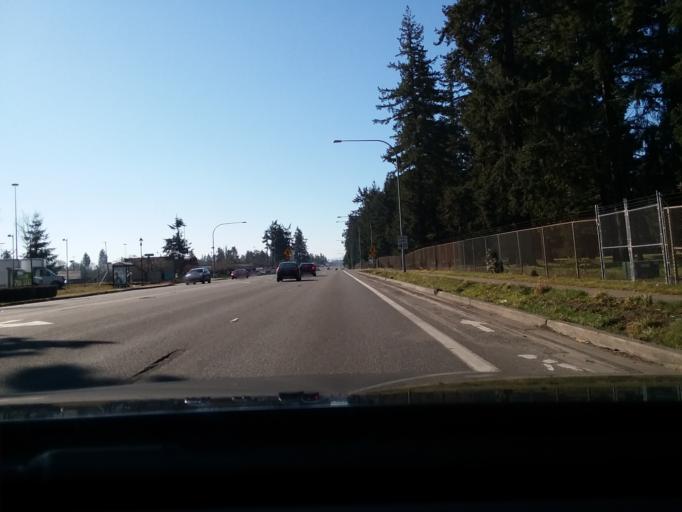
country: US
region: Washington
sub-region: Pierce County
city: Spanaway
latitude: 47.1166
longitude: -122.4350
